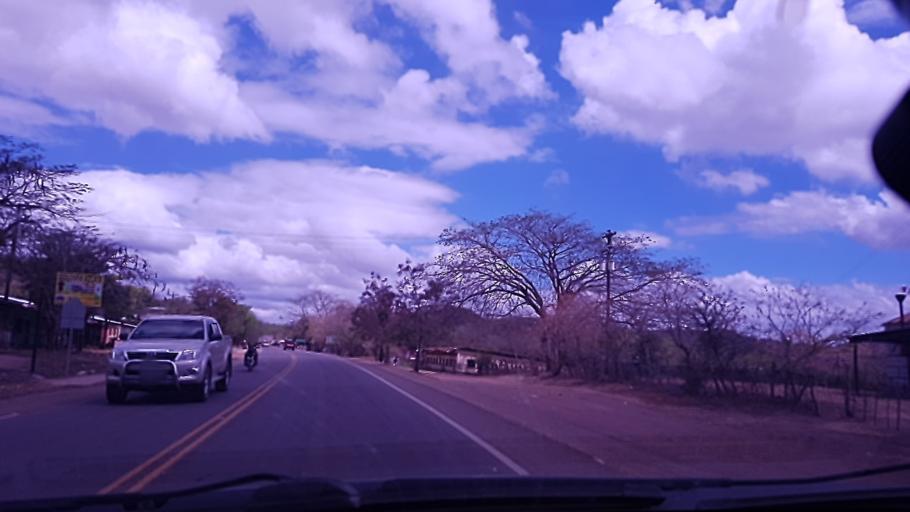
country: NI
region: Esteli
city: Condega
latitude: 13.3687
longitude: -86.3988
